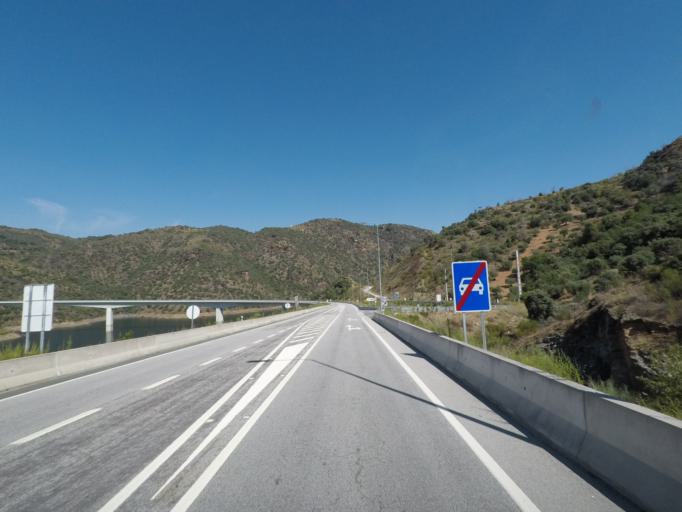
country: PT
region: Braganca
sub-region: Alfandega da Fe
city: Alfandega da Fe
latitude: 41.2835
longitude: -6.8708
